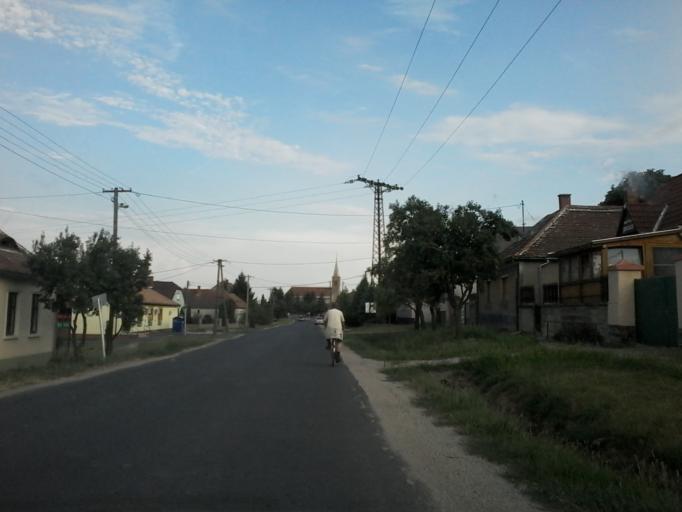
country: HU
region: Vas
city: Sarvar
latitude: 47.2118
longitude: 17.0190
